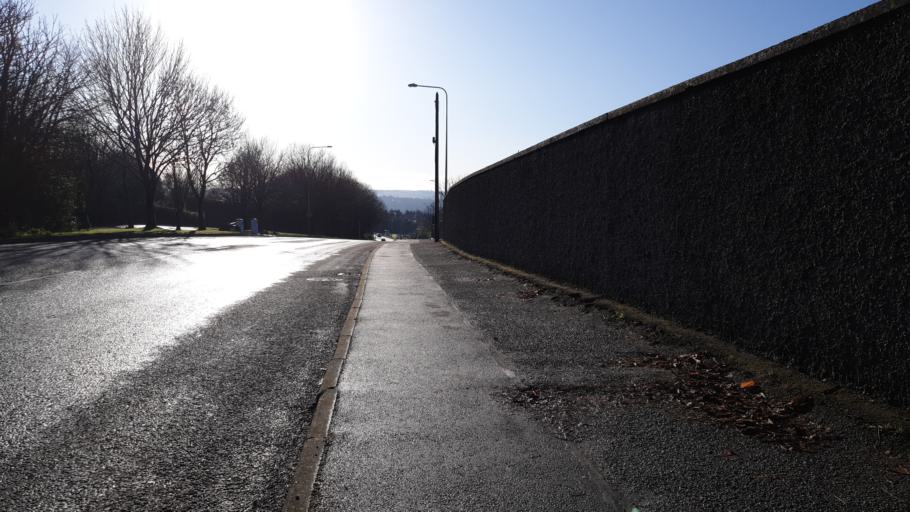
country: IE
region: Munster
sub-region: County Cork
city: Cork
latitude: 51.8904
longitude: -8.4334
